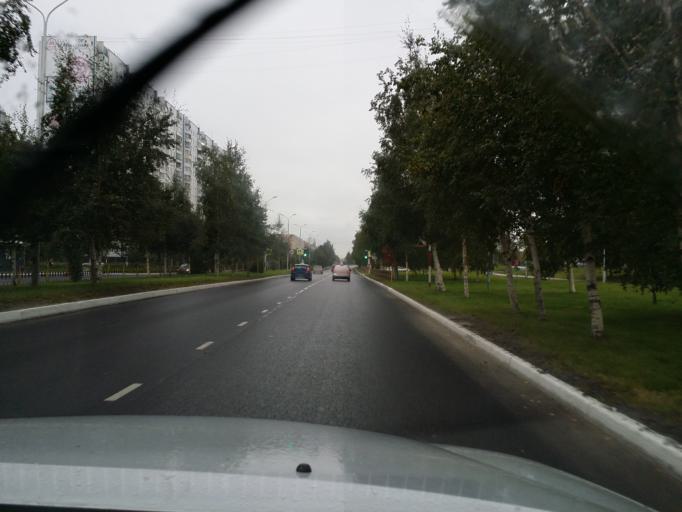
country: RU
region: Khanty-Mansiyskiy Avtonomnyy Okrug
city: Nizhnevartovsk
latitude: 60.9377
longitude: 76.5937
